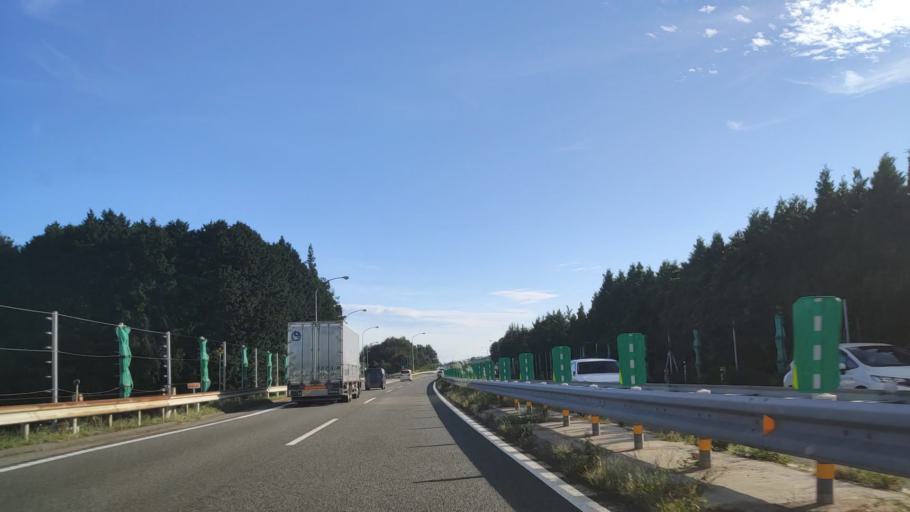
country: JP
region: Nagano
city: Iida
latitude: 35.6112
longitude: 137.8858
